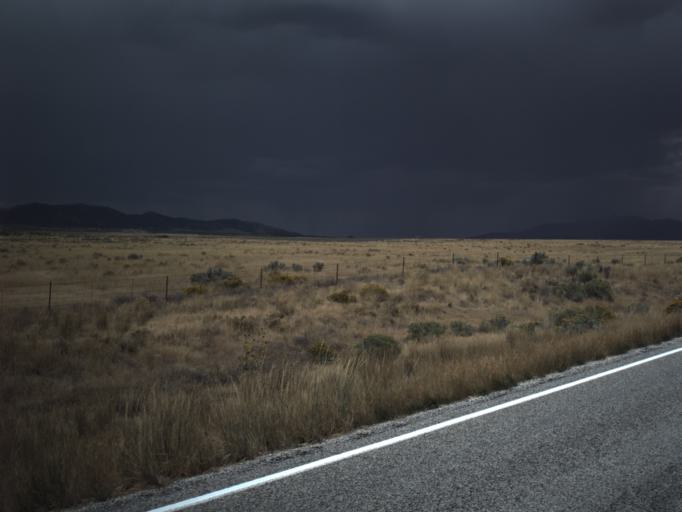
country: US
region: Idaho
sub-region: Minidoka County
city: Rupert
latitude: 41.8506
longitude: -113.1343
